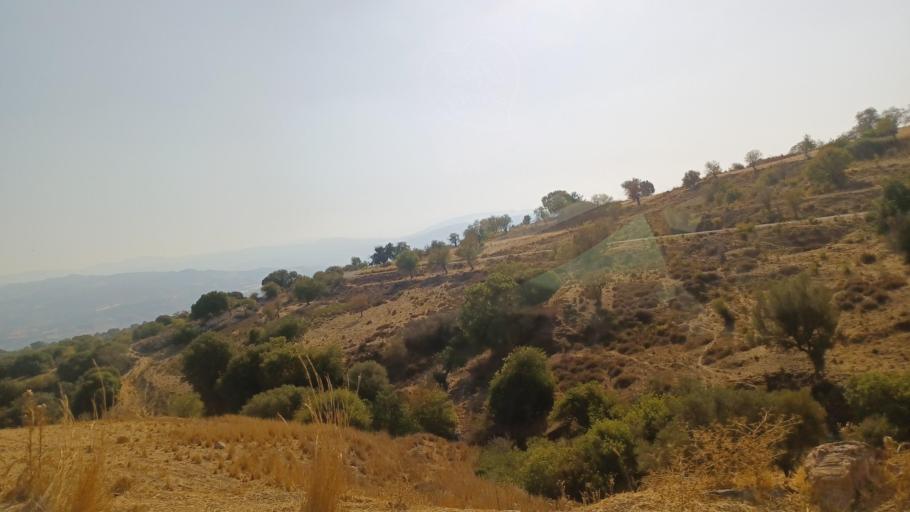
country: CY
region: Pafos
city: Polis
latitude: 34.9712
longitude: 32.4187
